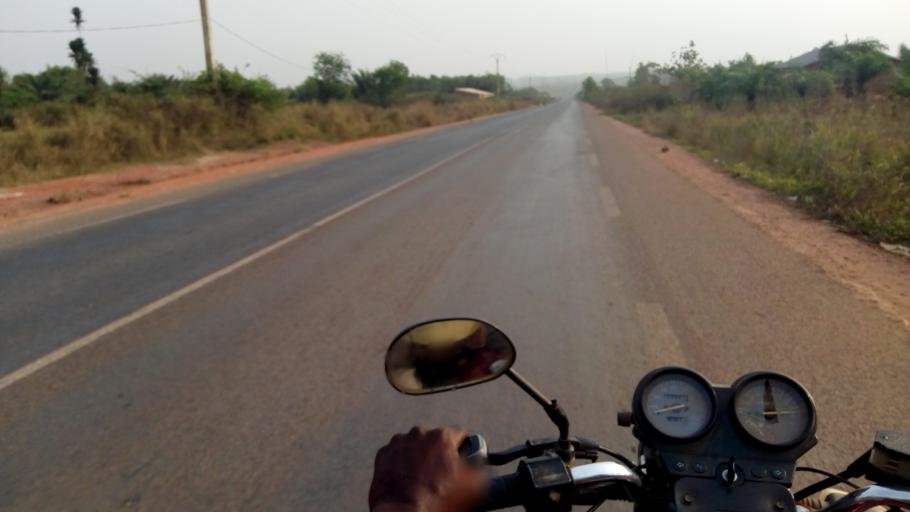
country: BJ
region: Atlantique
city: Hinvi
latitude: 6.7031
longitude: 2.2901
